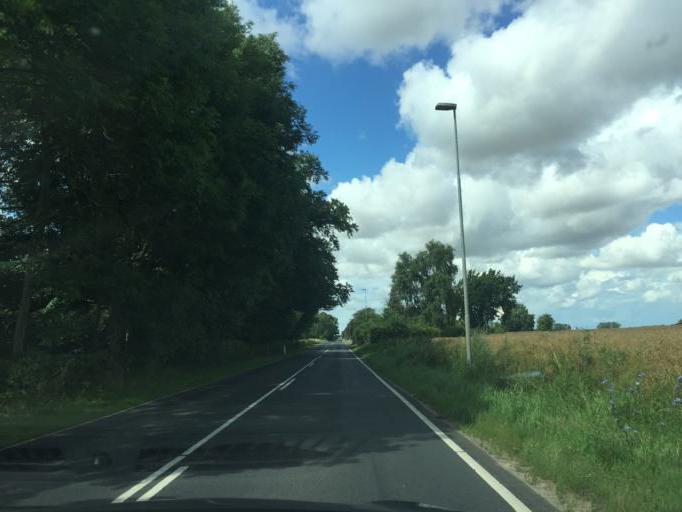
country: DK
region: South Denmark
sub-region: Odense Kommune
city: Stige
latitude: 55.4575
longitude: 10.3629
